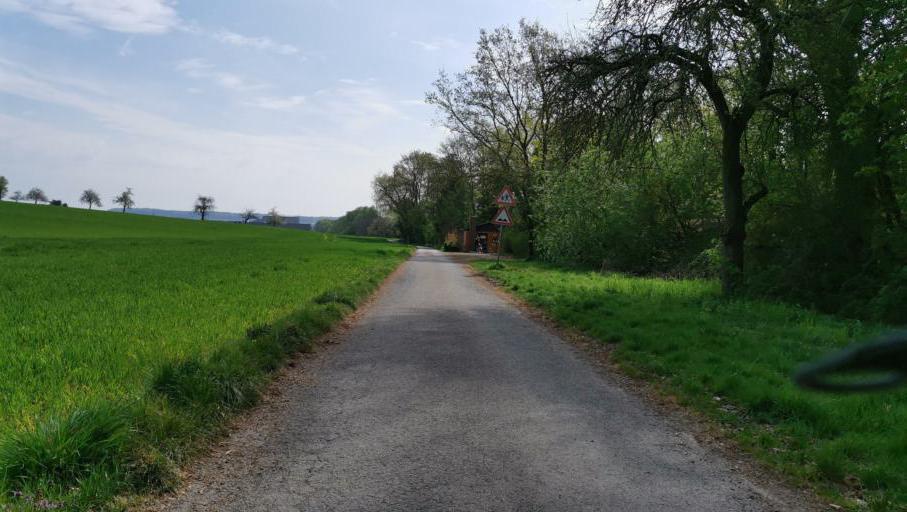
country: DE
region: Hesse
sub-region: Regierungsbezirk Darmstadt
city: Karben
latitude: 50.2425
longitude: 8.7431
